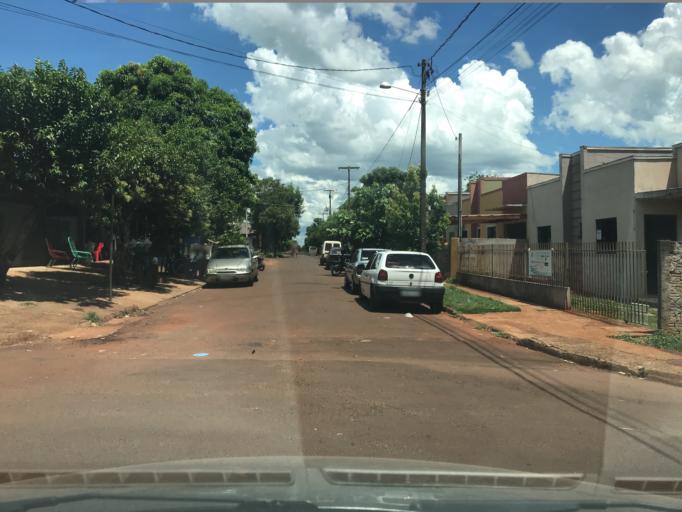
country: BR
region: Parana
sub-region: Palotina
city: Palotina
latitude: -24.2701
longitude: -53.8463
